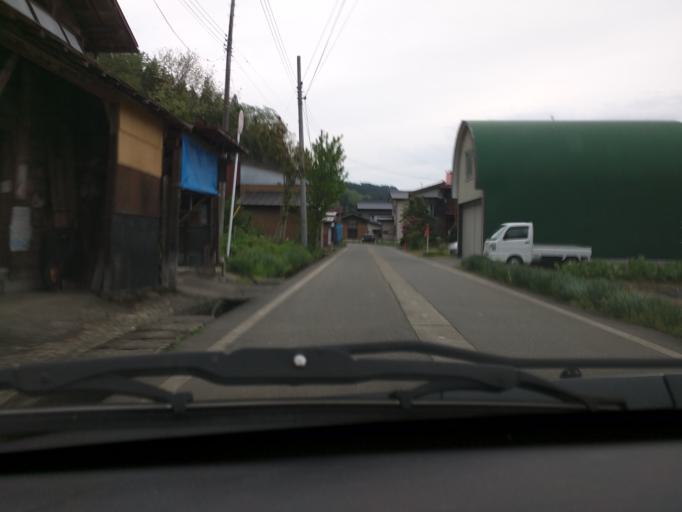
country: JP
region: Niigata
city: Muikamachi
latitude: 37.2135
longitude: 138.9501
